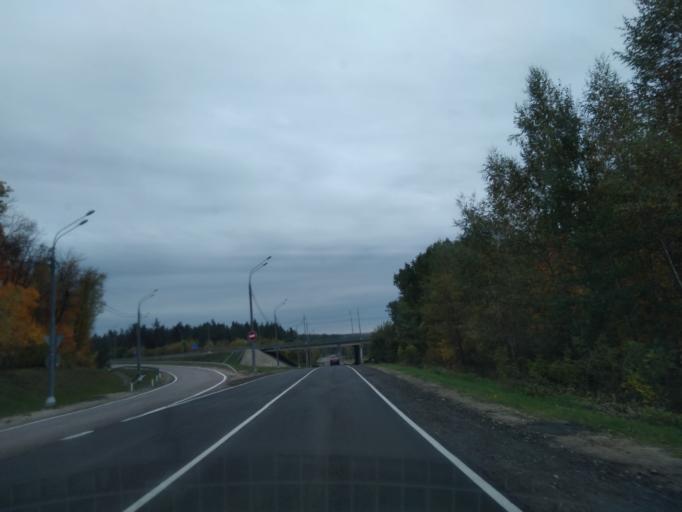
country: RU
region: Lipetsk
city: Zadonsk
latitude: 52.3710
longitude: 38.9179
